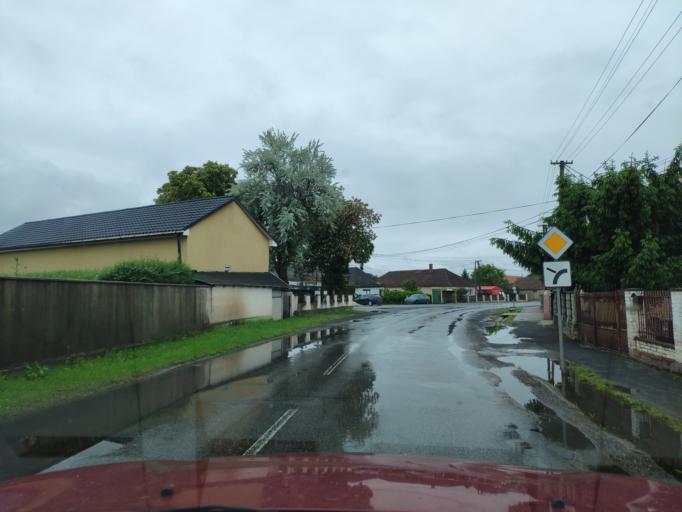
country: SK
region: Kosicky
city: Cierna nad Tisou
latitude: 48.4112
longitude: 22.0570
